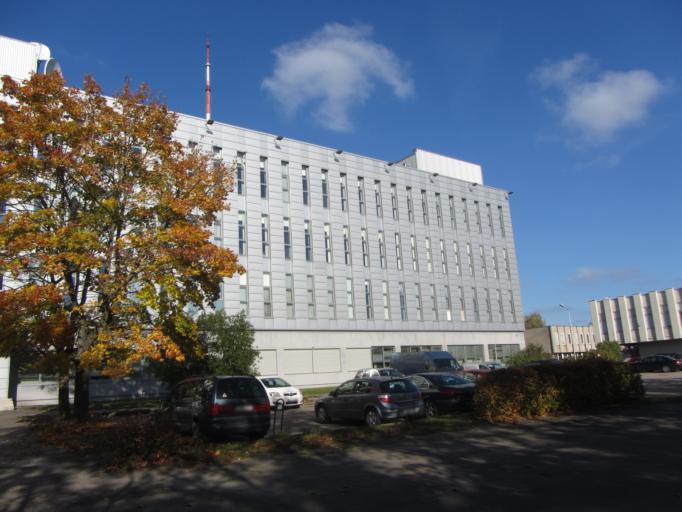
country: LT
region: Vilnius County
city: Lazdynai
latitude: 54.6832
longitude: 25.2114
